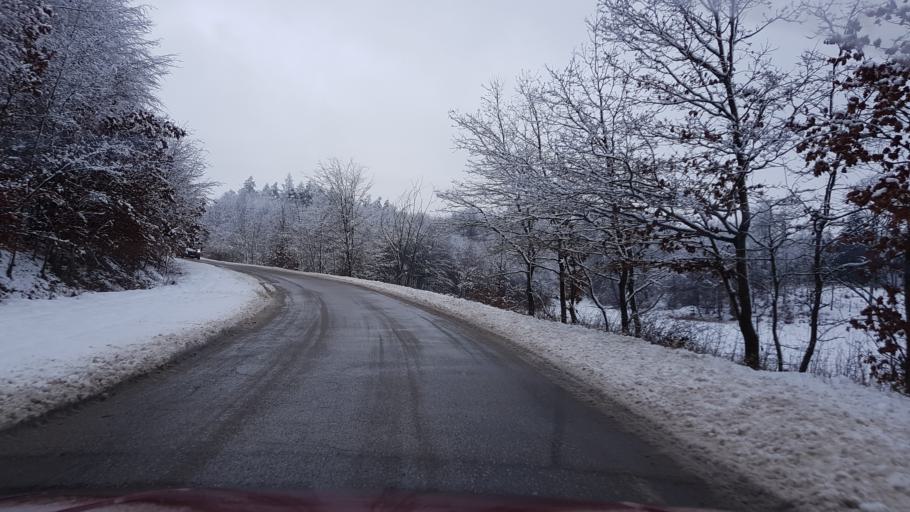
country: PL
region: West Pomeranian Voivodeship
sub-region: Powiat drawski
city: Zlocieniec
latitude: 53.5048
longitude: 15.9994
